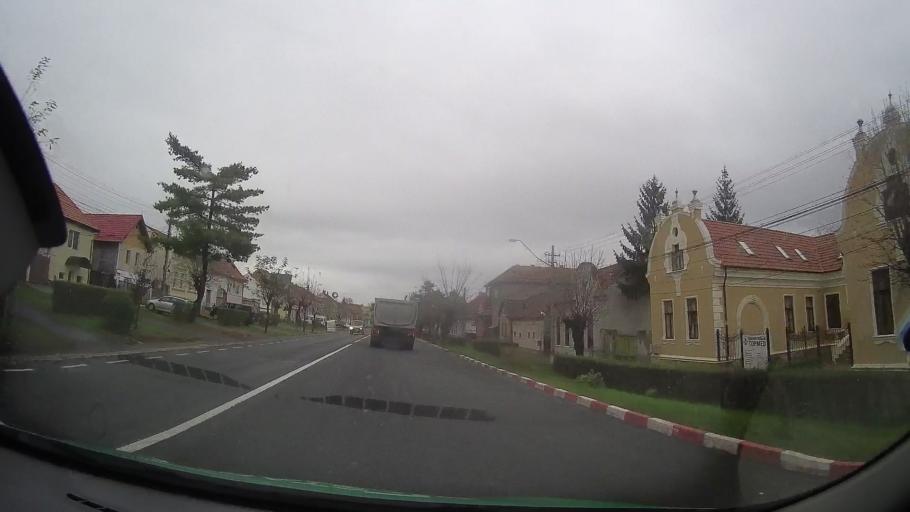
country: RO
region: Mures
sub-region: Municipiul Reghin
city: Reghin
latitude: 46.7738
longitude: 24.6925
